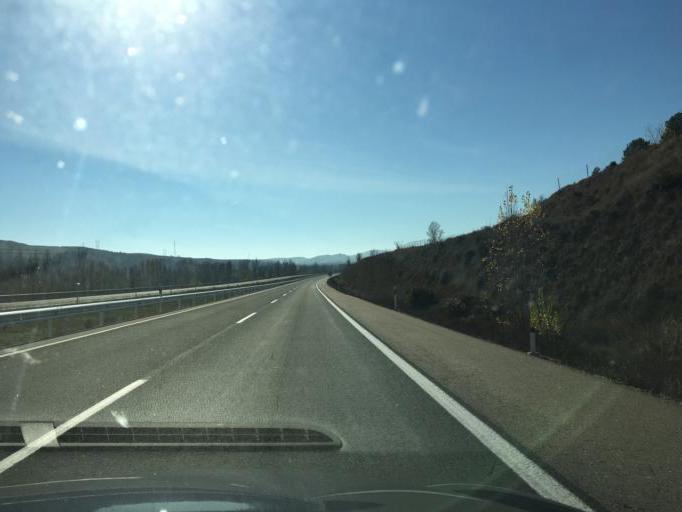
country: ES
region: Castille and Leon
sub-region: Provincia de Burgos
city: Pradanos de Bureba
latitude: 42.5098
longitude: -3.3470
